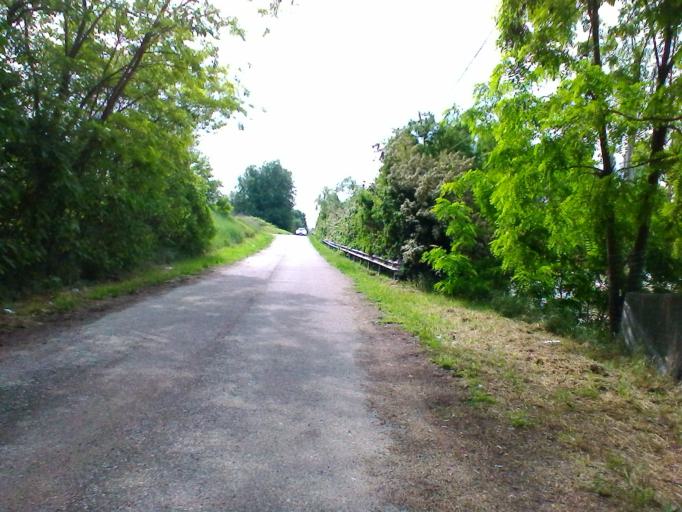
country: IT
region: Lombardy
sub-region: Provincia di Mantova
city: Cerese
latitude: 45.1366
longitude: 10.8036
